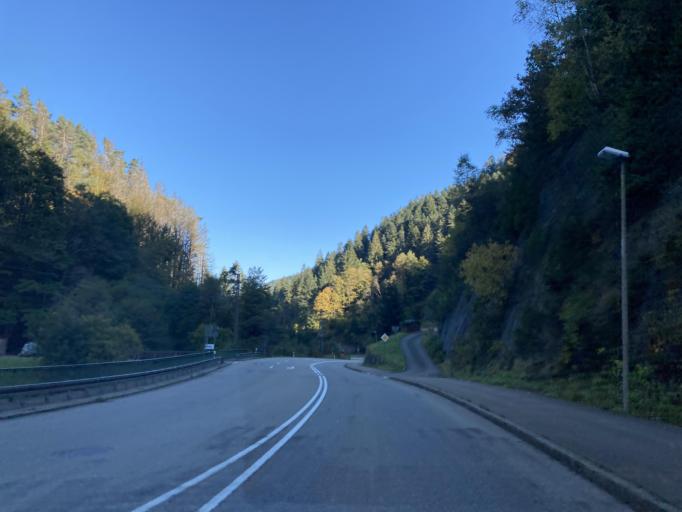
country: DE
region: Baden-Wuerttemberg
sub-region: Freiburg Region
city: Triberg im Schwarzwald
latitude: 48.1504
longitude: 8.2397
